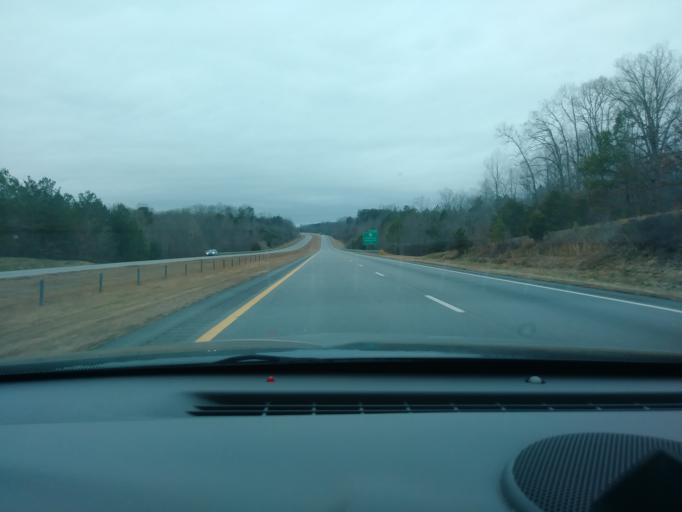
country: US
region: North Carolina
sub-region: Yadkin County
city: Yadkinville
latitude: 36.1175
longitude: -80.7477
